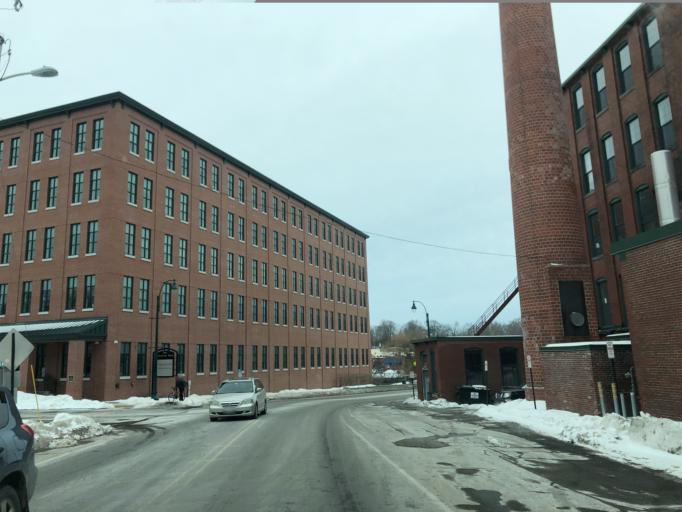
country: US
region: Maine
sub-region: Cumberland County
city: Westbrook
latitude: 43.6788
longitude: -70.3676
